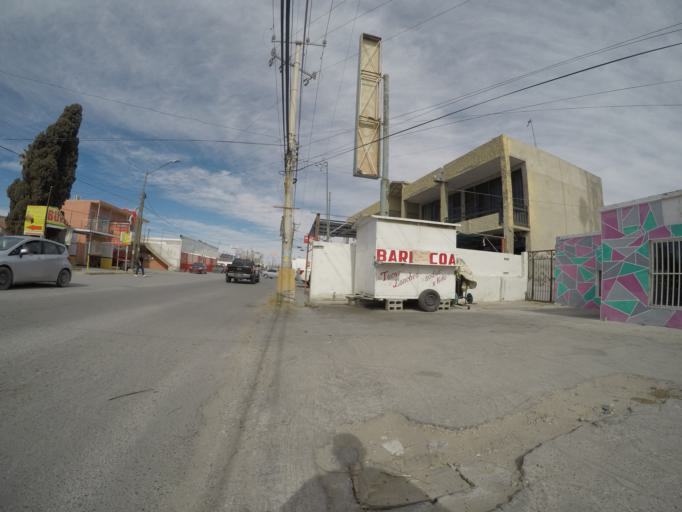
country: MX
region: Chihuahua
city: Ciudad Juarez
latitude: 31.7147
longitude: -106.4332
